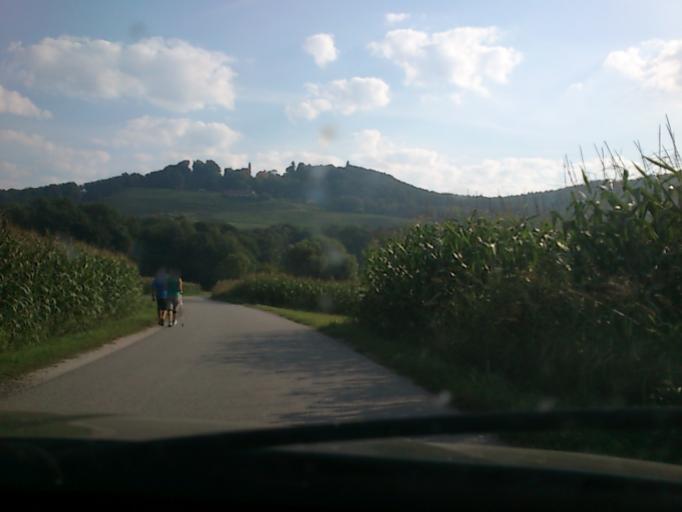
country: SI
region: Starse
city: Starse
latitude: 46.4793
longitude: 15.7873
